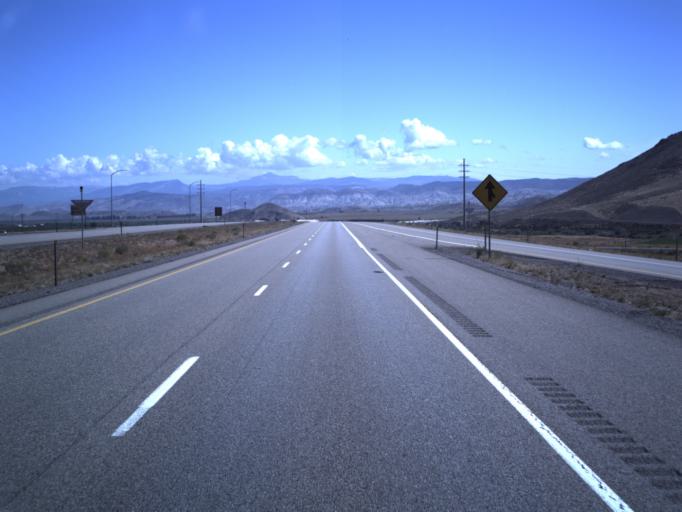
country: US
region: Utah
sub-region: Sevier County
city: Aurora
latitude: 38.8747
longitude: -111.9629
